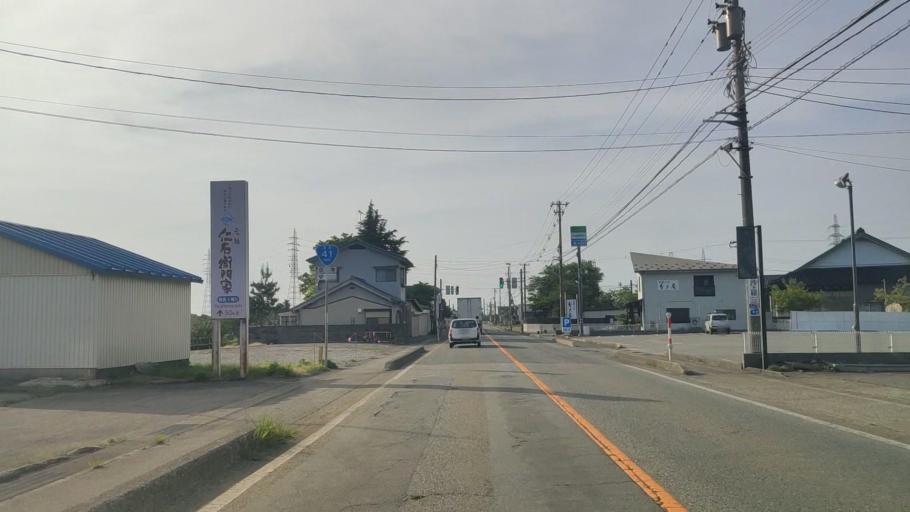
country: JP
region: Toyama
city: Yatsuomachi-higashikumisaka
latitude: 36.5626
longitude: 137.2136
